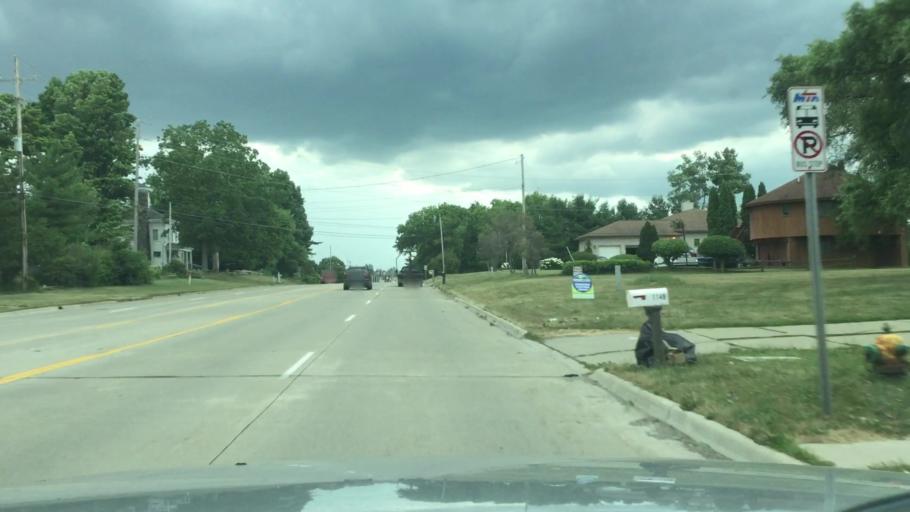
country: US
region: Michigan
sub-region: Genesee County
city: Swartz Creek
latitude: 43.0208
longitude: -83.7733
